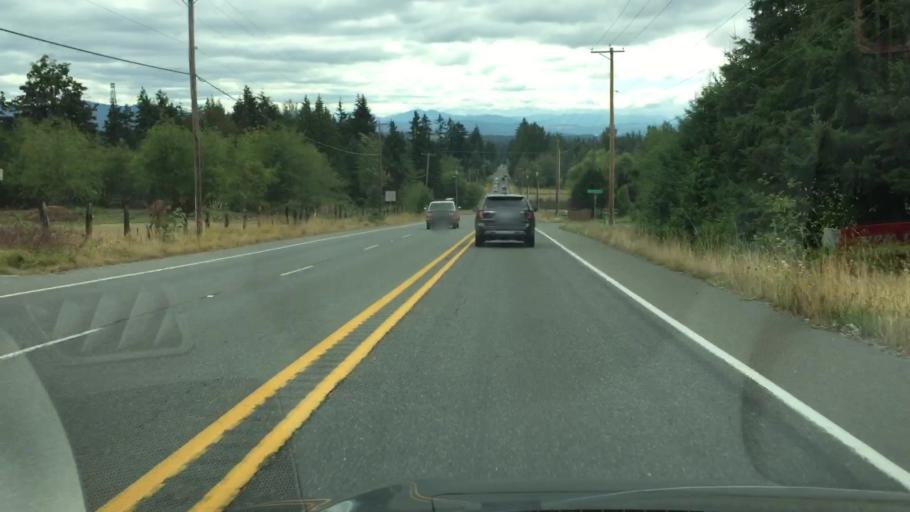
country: US
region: Washington
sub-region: Pierce County
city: Graham
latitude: 47.0240
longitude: -122.2962
